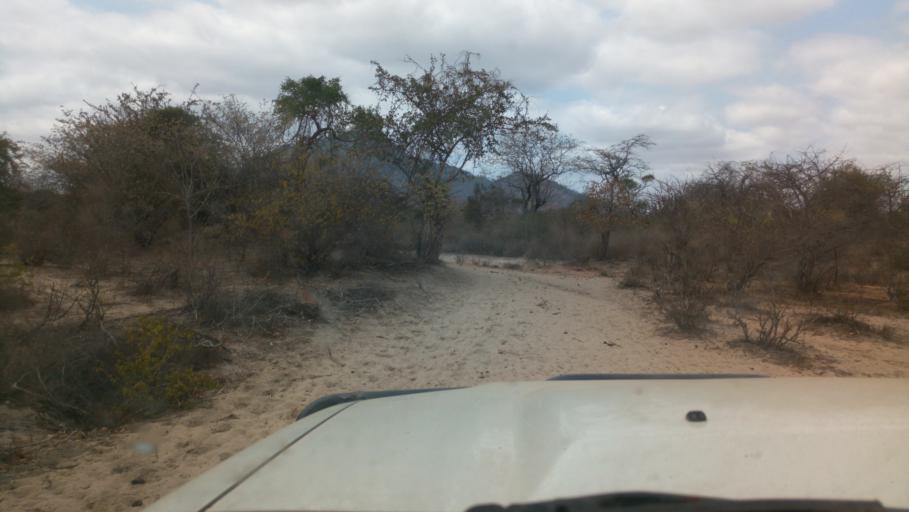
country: KE
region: Kitui
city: Kitui
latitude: -1.8487
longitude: 38.3808
